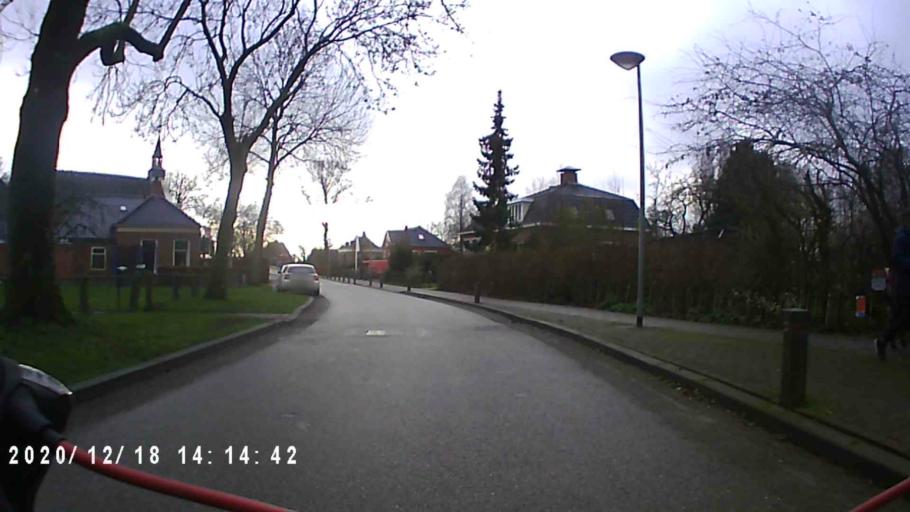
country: NL
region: Groningen
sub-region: Gemeente Bedum
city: Bedum
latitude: 53.2682
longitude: 6.6515
